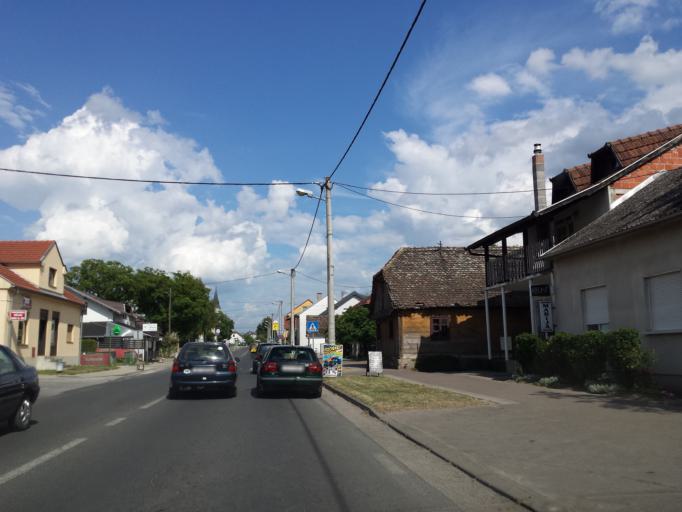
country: HR
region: Zagrebacka
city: Brckovljani
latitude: 45.8050
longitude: 16.2387
